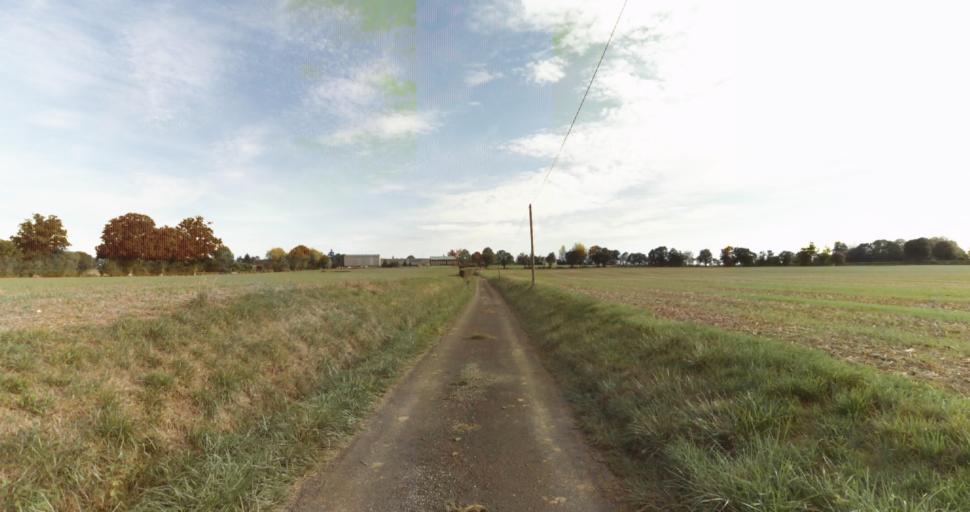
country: FR
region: Lower Normandy
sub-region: Departement de l'Orne
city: Gace
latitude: 48.7119
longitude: 0.2766
